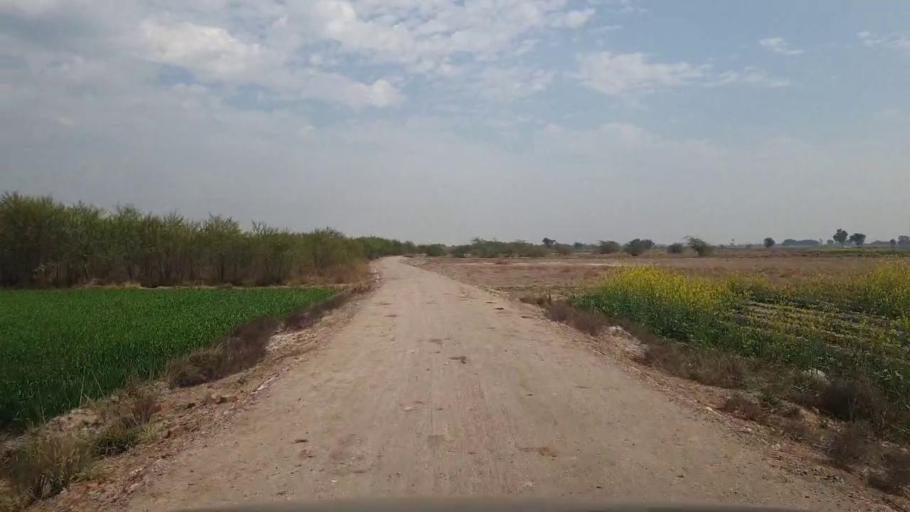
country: PK
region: Sindh
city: Sakrand
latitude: 26.0222
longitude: 68.3994
